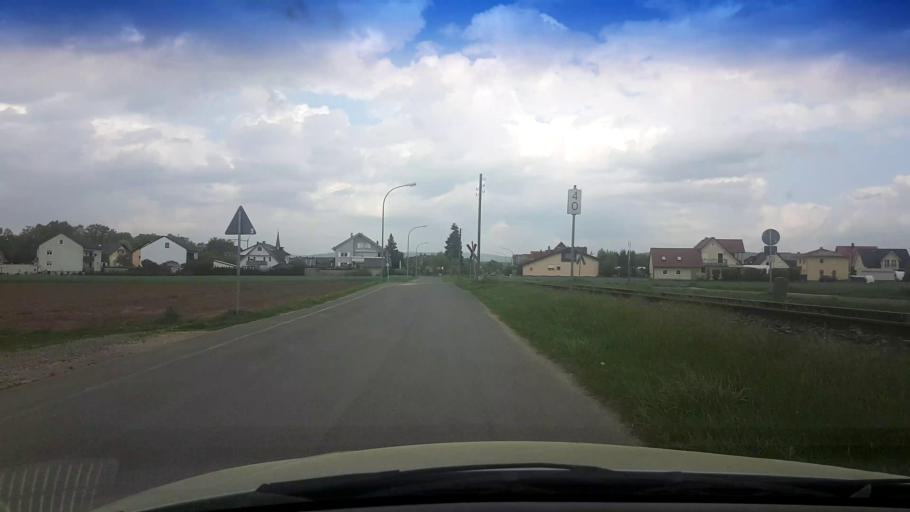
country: DE
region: Bavaria
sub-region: Upper Franconia
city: Pettstadt
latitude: 49.8263
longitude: 10.9200
